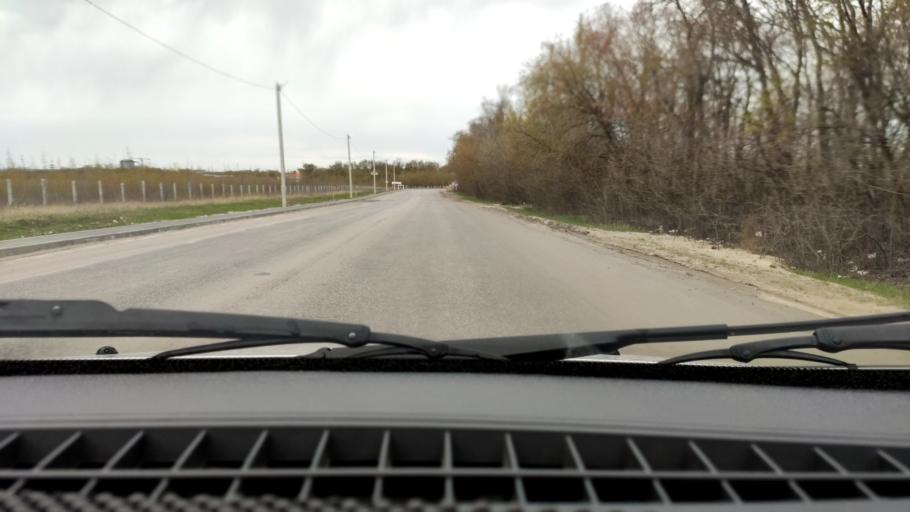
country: RU
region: Voronezj
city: Novaya Usman'
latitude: 51.6313
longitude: 39.3335
